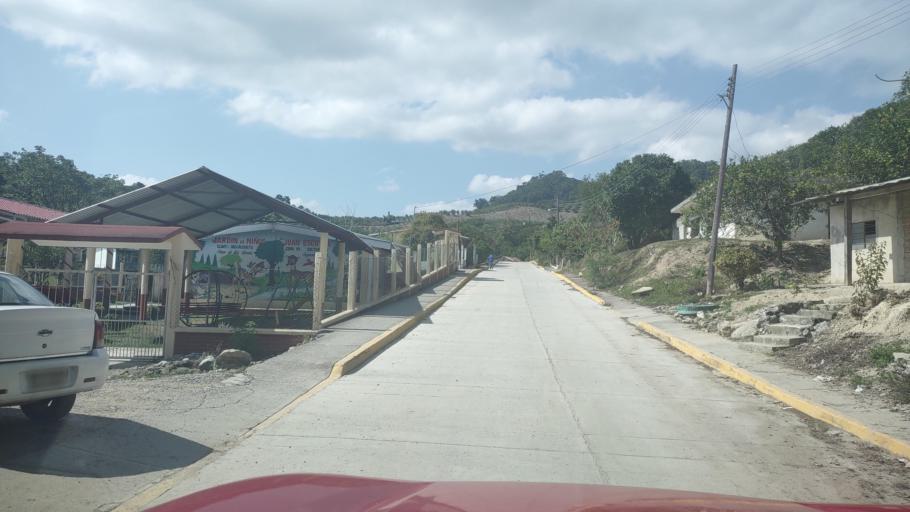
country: MX
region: Veracruz
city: Agua Dulce
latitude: 20.2949
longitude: -97.1498
